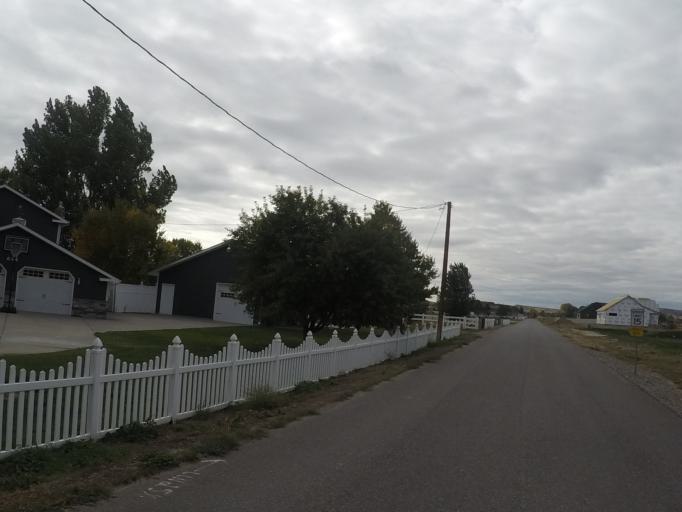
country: US
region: Montana
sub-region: Yellowstone County
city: Laurel
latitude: 45.7769
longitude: -108.6594
